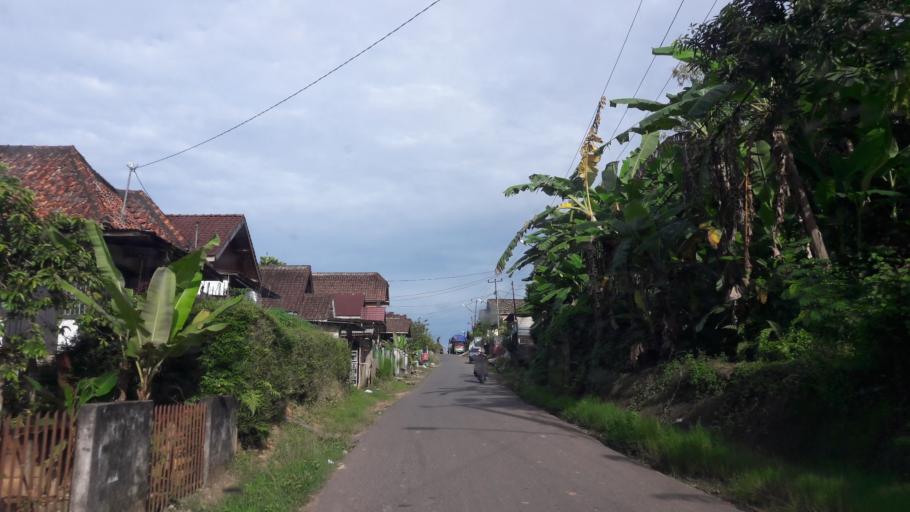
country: ID
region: South Sumatra
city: Gunungmegang Dalam
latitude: -3.2664
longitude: 103.8152
